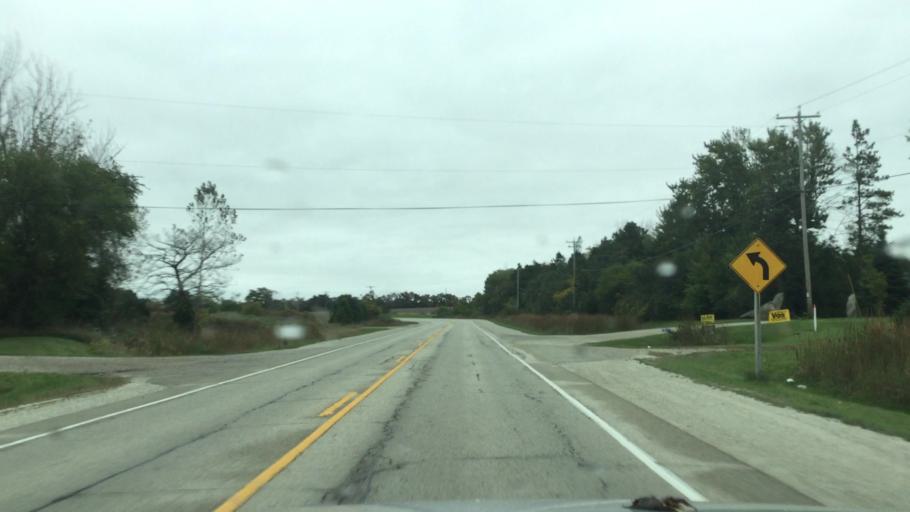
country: US
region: Wisconsin
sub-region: Racine County
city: Eagle Lake
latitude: 42.7404
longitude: -88.1015
